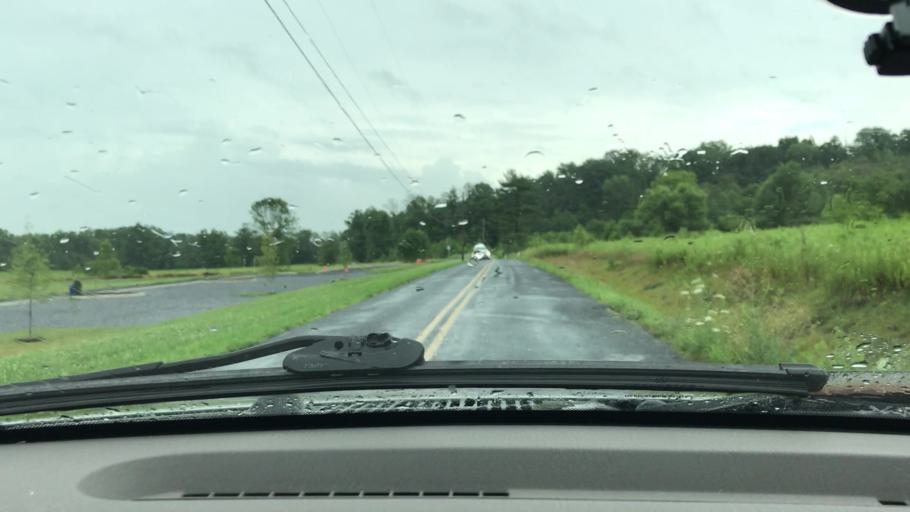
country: US
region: Pennsylvania
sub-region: Lancaster County
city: Elizabethtown
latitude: 40.1850
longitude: -76.5980
